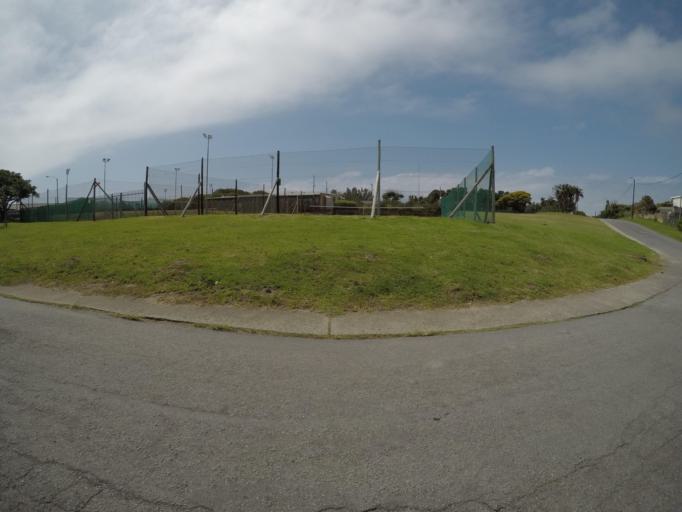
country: ZA
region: Eastern Cape
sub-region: Buffalo City Metropolitan Municipality
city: East London
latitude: -32.9375
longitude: 28.0238
